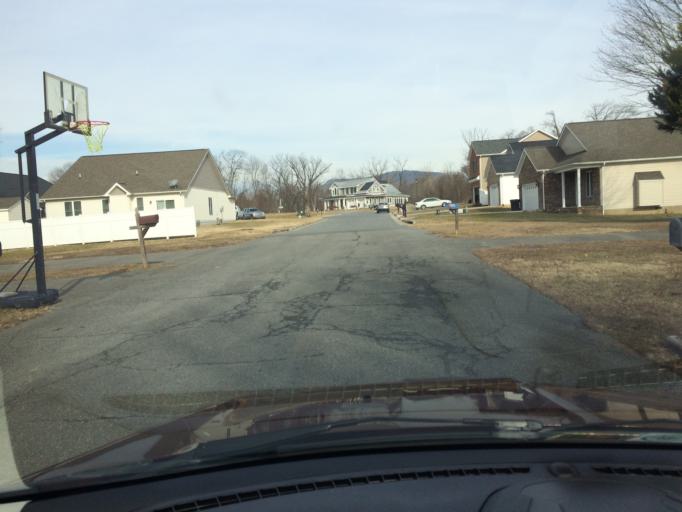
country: US
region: Virginia
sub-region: Roanoke County
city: Hollins
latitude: 37.3293
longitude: -79.9329
